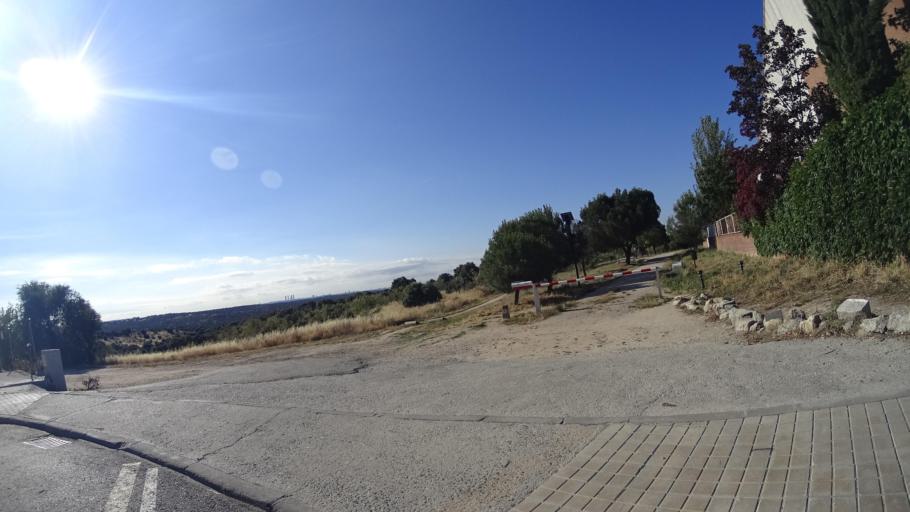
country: ES
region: Madrid
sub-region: Provincia de Madrid
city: Las Matas
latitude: 40.5535
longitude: -3.8872
